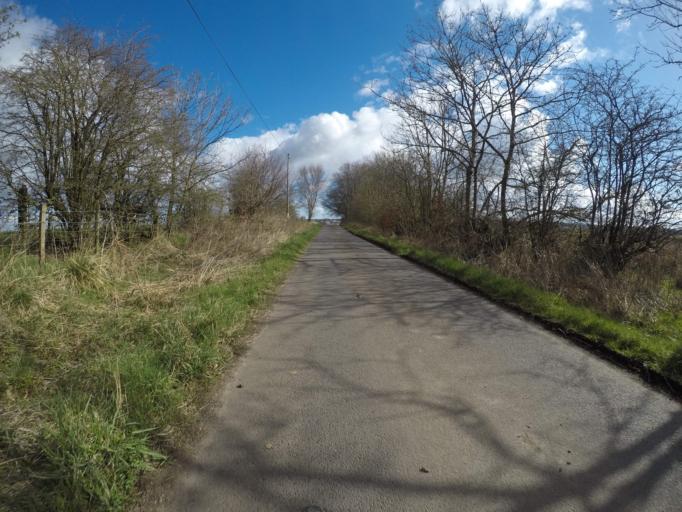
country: GB
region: Scotland
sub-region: North Ayrshire
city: Beith
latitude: 55.7163
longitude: -4.6342
